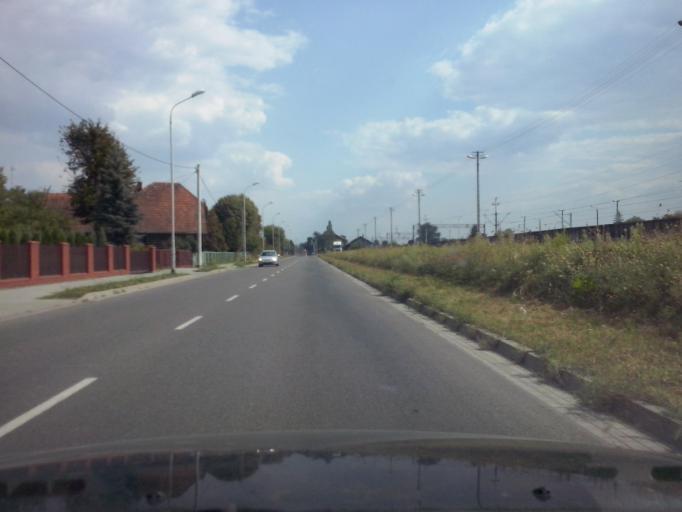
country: PL
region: Subcarpathian Voivodeship
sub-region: Powiat nizanski
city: Nisko
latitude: 50.5159
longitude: 22.1379
